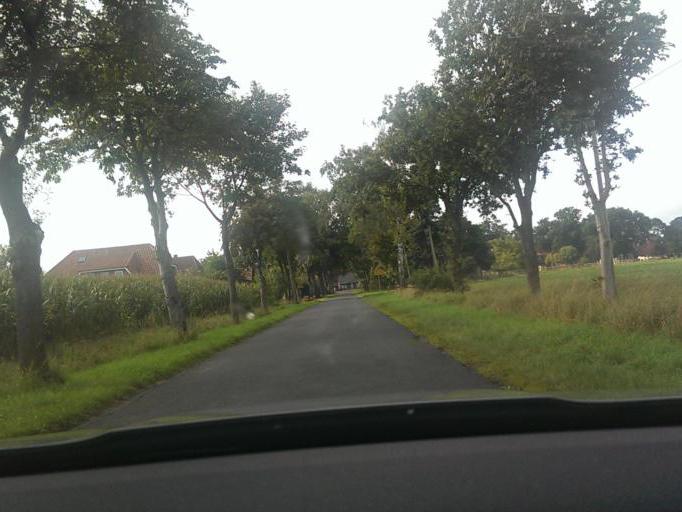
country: DE
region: Lower Saxony
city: Elze
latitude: 52.5701
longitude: 9.7648
